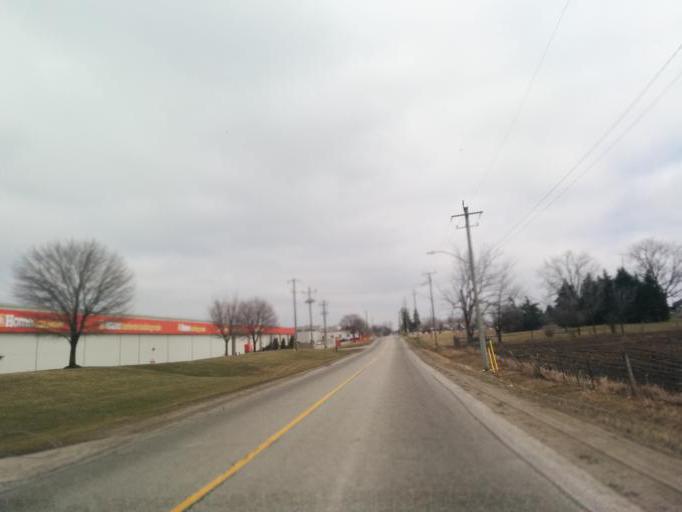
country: CA
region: Ontario
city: Waterloo
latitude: 43.5336
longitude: -80.5626
